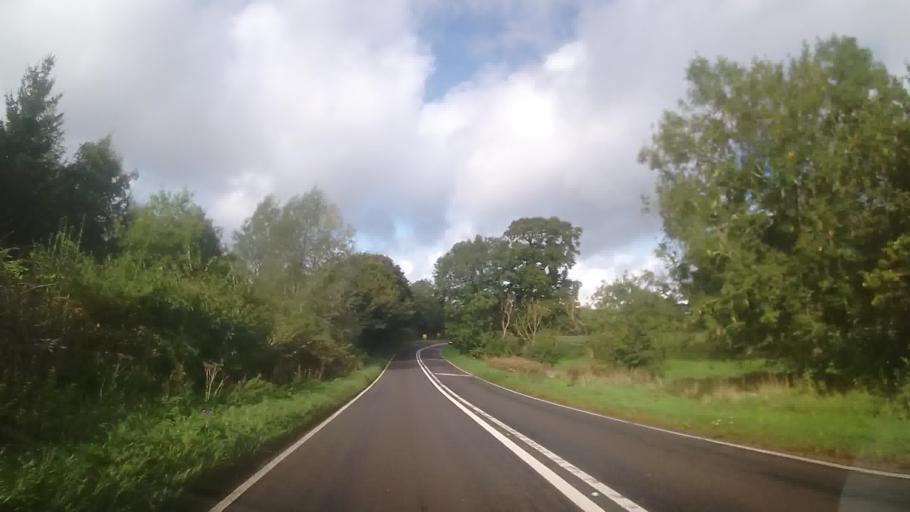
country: GB
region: England
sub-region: Oxfordshire
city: Chipping Norton
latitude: 51.9502
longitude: -1.5853
